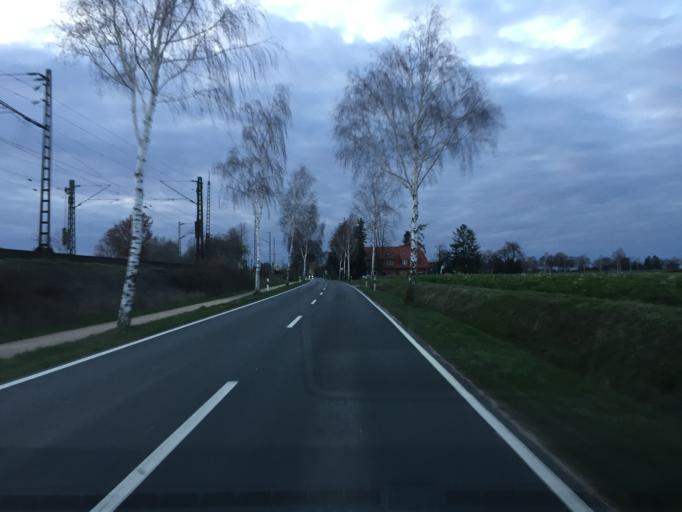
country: DE
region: Lower Saxony
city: Steimbke
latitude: 52.5754
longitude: 9.4071
